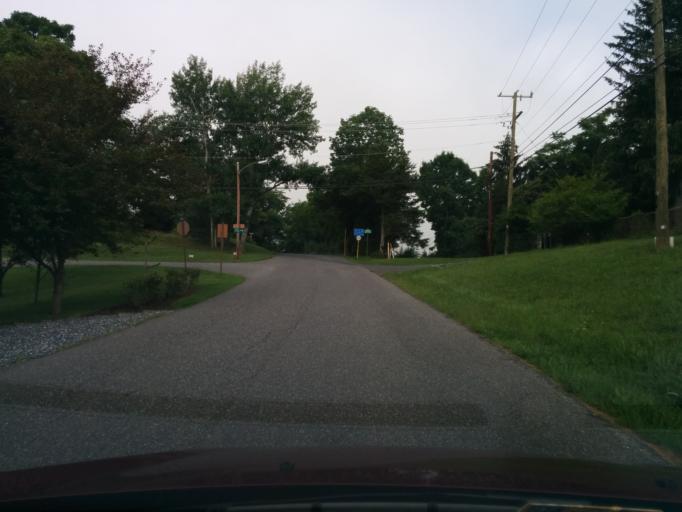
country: US
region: Virginia
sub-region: City of Lexington
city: Lexington
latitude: 37.7856
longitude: -79.4610
